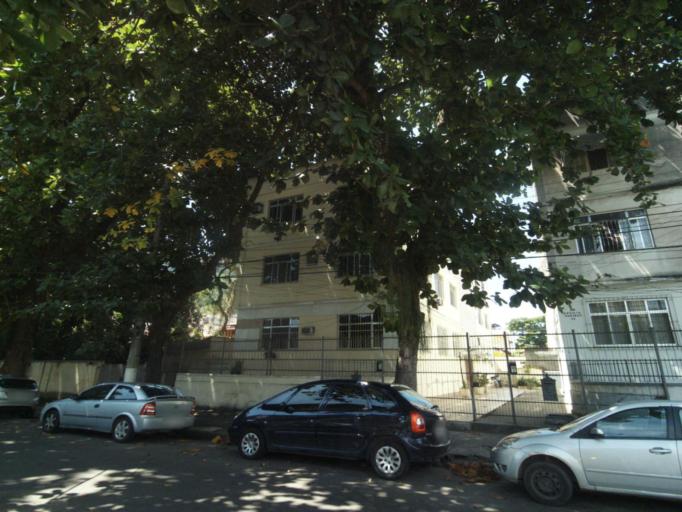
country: BR
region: Rio de Janeiro
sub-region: Niteroi
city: Niteroi
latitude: -22.9152
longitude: -43.0937
